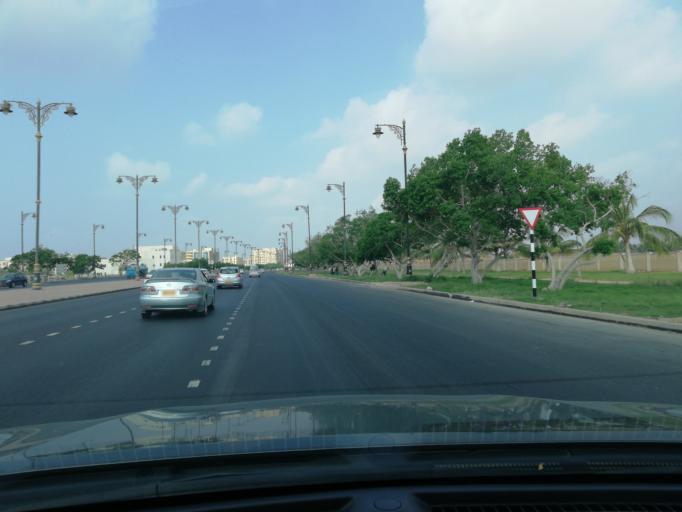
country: OM
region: Zufar
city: Salalah
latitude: 17.0244
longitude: 54.0896
